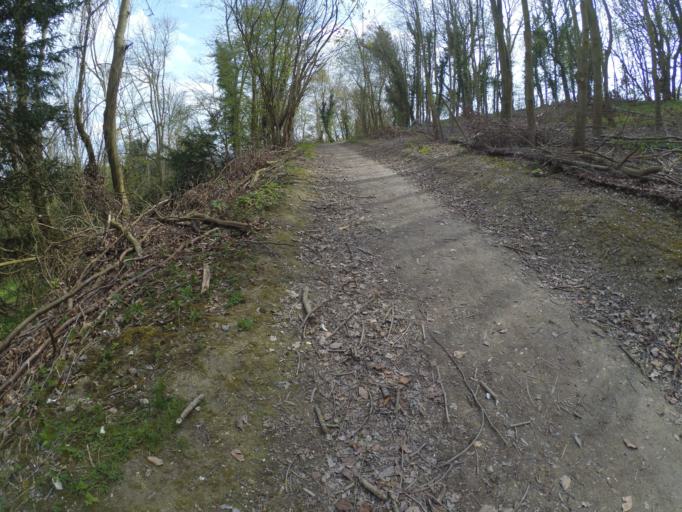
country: GB
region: England
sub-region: West Sussex
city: Arundel
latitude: 50.8808
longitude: -0.5542
